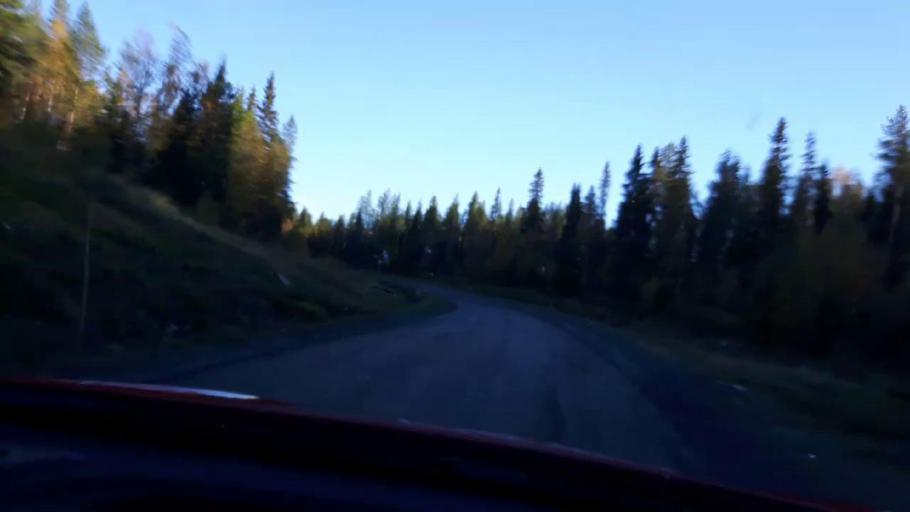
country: SE
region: Jaemtland
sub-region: OEstersunds Kommun
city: Lit
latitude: 63.5832
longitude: 14.8552
